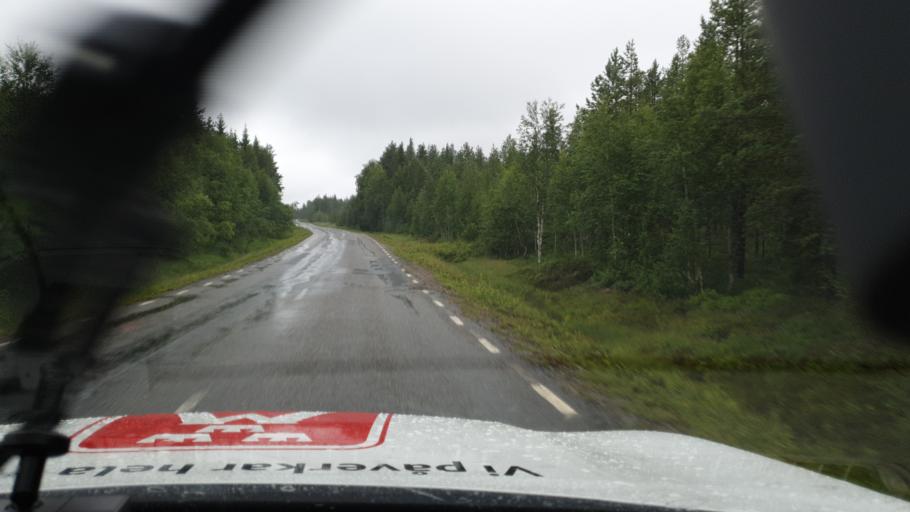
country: SE
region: Vaesterbotten
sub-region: Skelleftea Kommun
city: Langsele
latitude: 65.0278
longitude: 20.2045
